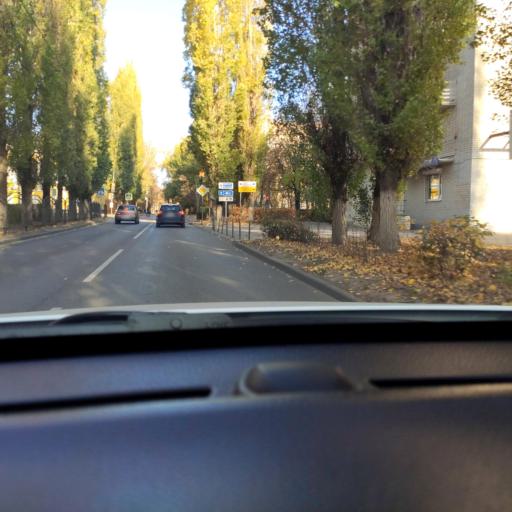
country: RU
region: Voronezj
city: Voronezh
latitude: 51.7145
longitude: 39.2277
